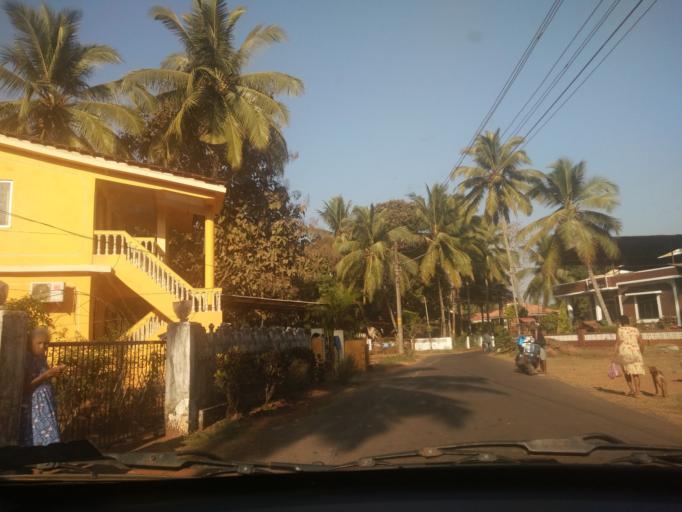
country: IN
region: Goa
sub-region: South Goa
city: Colva
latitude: 15.3025
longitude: 73.9151
